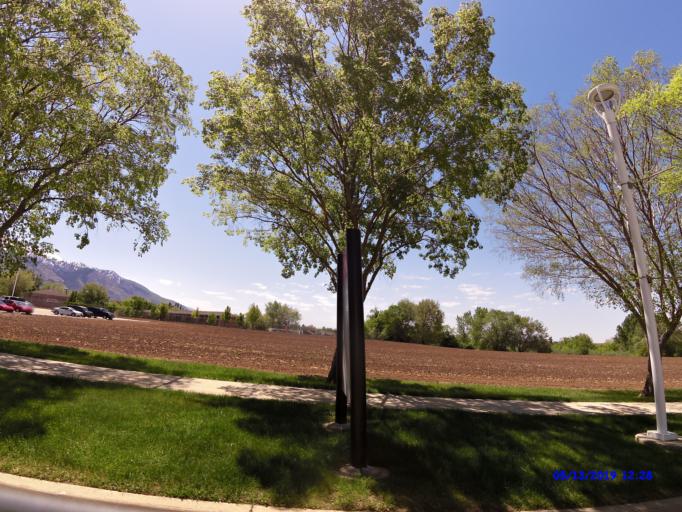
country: US
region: Utah
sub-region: Weber County
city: Harrisville
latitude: 41.2623
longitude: -111.9643
